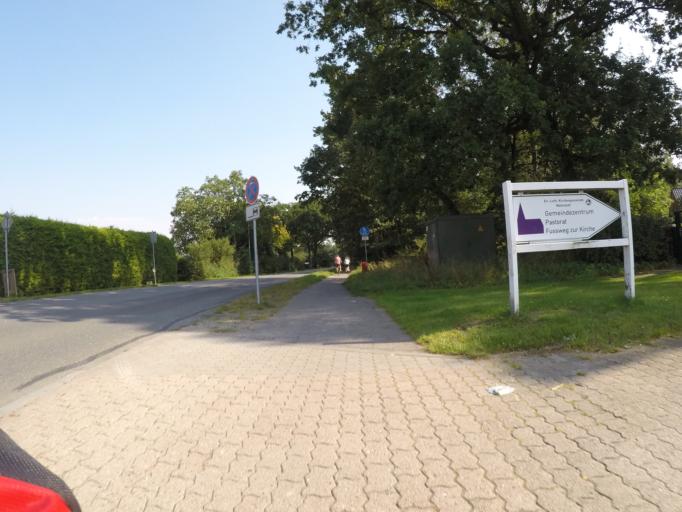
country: DE
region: Schleswig-Holstein
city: Wahlstedt
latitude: 53.9507
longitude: 10.2203
